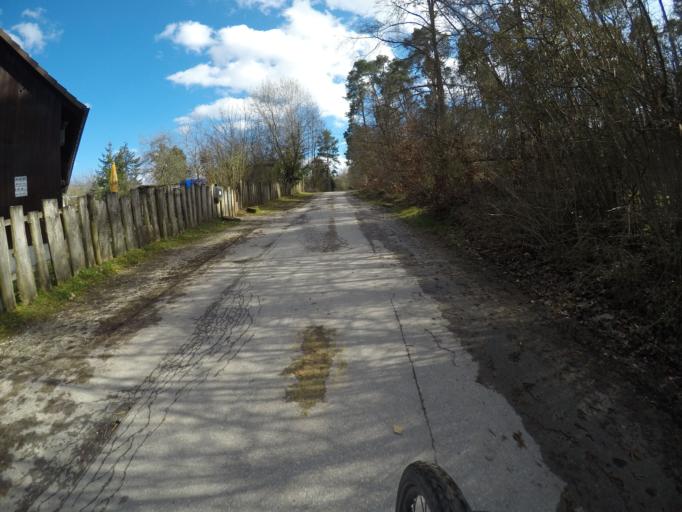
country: DE
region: Baden-Wuerttemberg
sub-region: Regierungsbezirk Stuttgart
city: Leinfelden-Echterdingen
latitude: 48.6792
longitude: 9.1523
